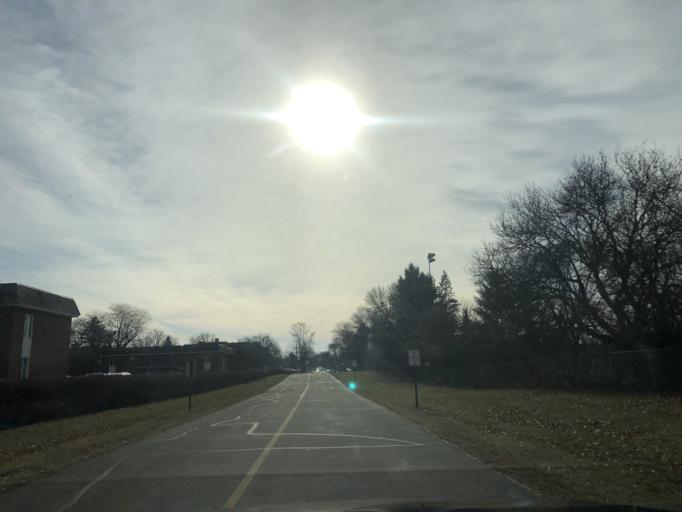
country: US
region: Illinois
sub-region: DuPage County
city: Downers Grove
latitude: 41.8131
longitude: -88.0149
